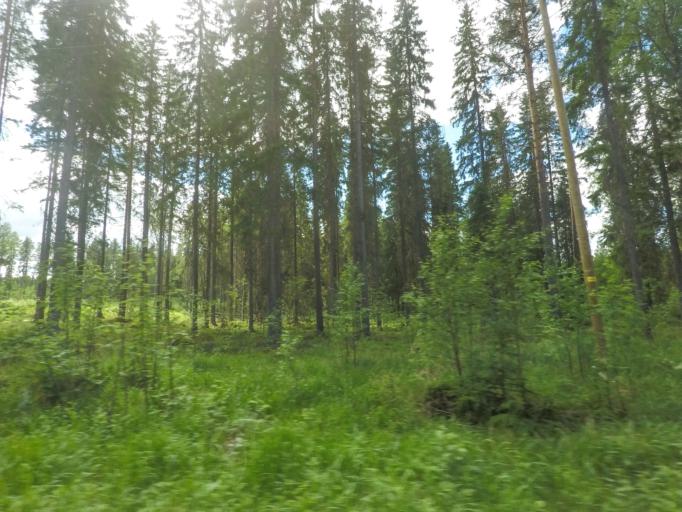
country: FI
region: Central Finland
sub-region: Jyvaeskylae
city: Hankasalmi
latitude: 62.4065
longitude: 26.6535
